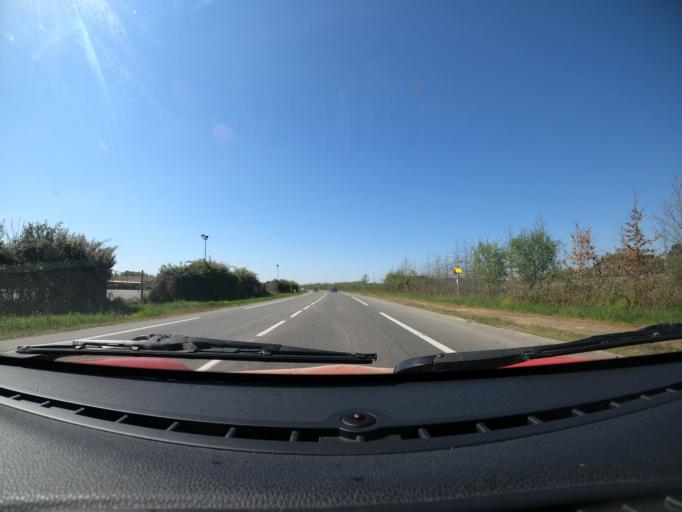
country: FR
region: Aquitaine
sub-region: Departement des Pyrenees-Atlantiques
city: Lescar
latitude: 43.3440
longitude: -0.4167
